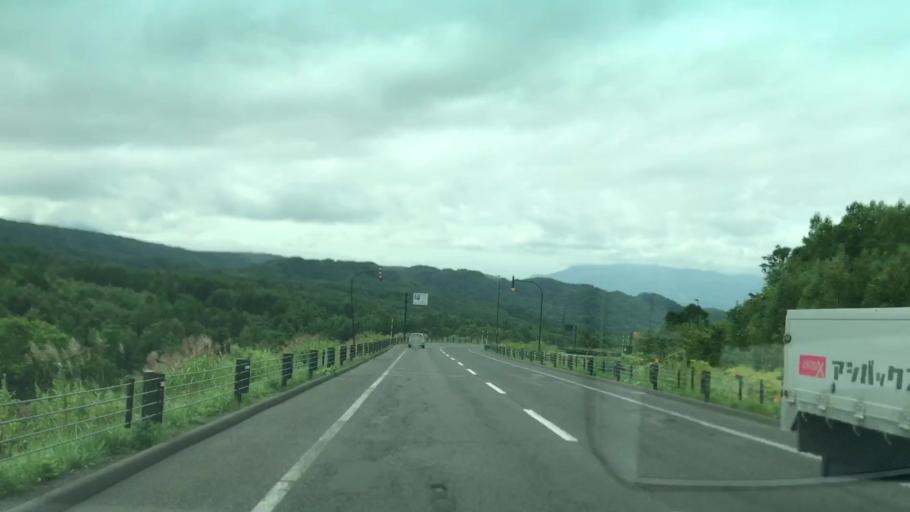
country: JP
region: Hokkaido
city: Niseko Town
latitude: 42.9540
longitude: 140.8630
